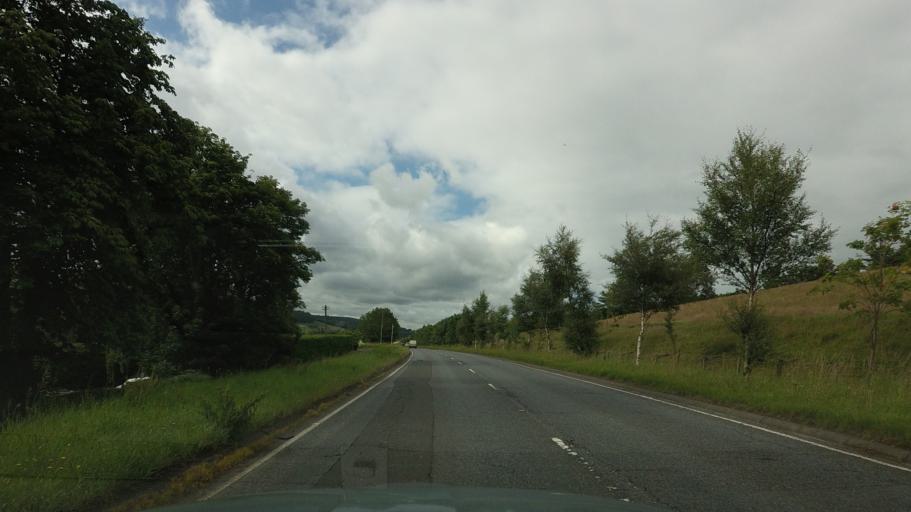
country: GB
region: Scotland
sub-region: The Scottish Borders
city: Peebles
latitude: 55.6676
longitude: -3.1965
